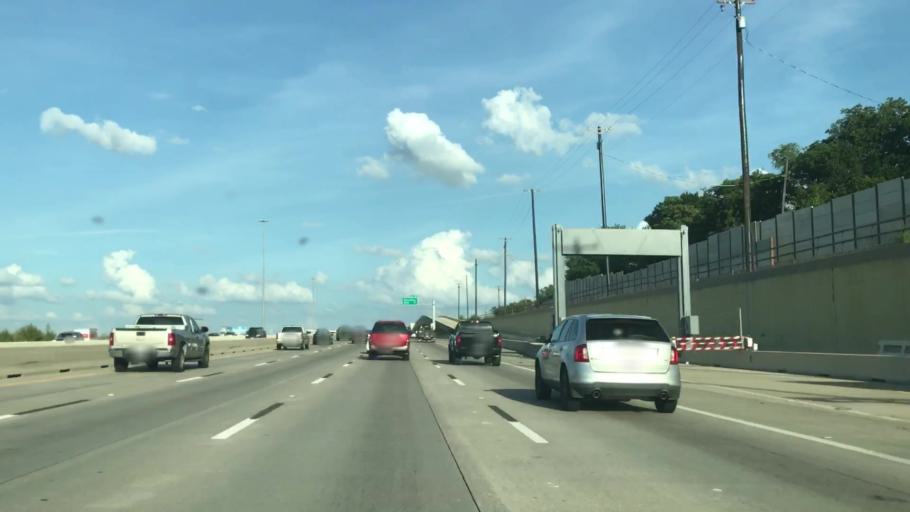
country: US
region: Texas
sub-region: Dallas County
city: Grand Prairie
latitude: 32.7590
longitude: -96.9799
